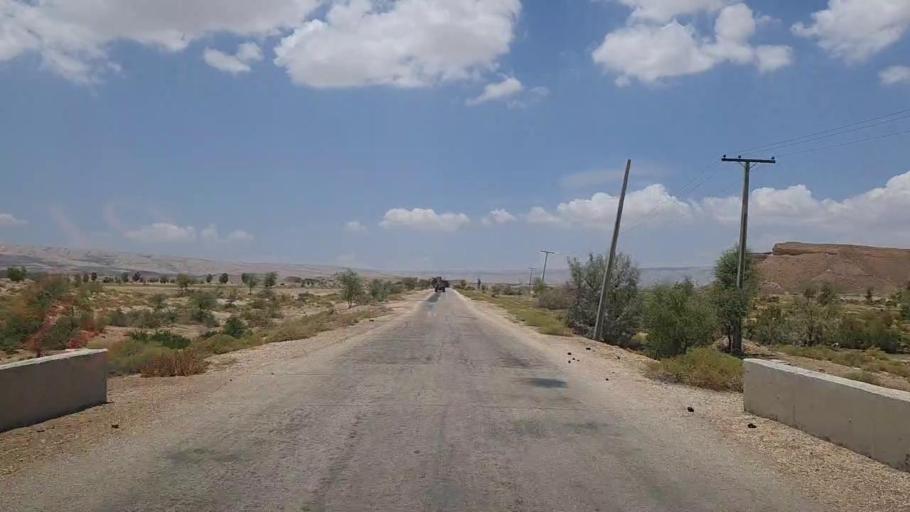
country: PK
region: Sindh
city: Sehwan
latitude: 26.3172
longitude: 67.6448
